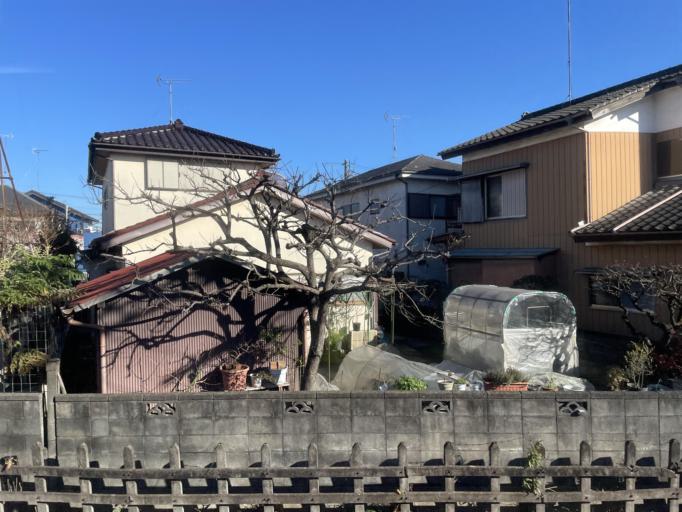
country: JP
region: Saitama
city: Satte
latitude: 36.0806
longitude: 139.7156
